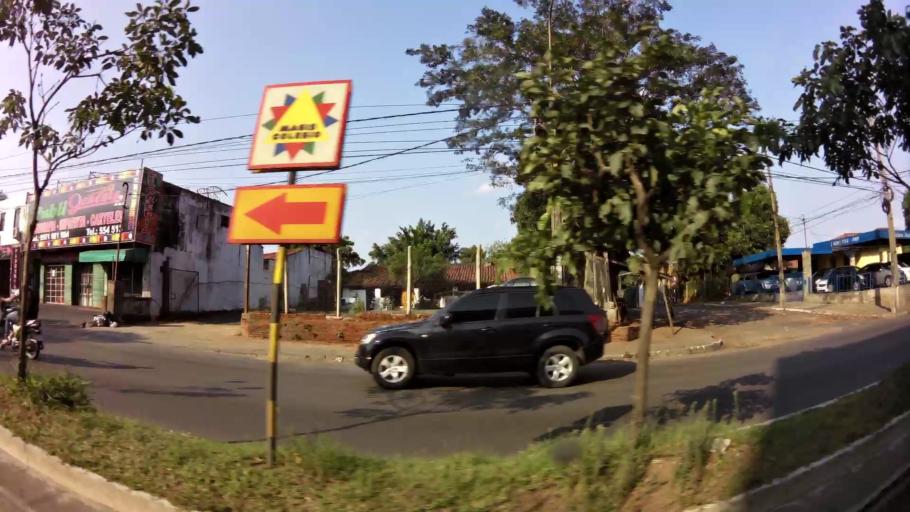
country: PY
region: Central
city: Lambare
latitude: -25.3286
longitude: -57.5943
